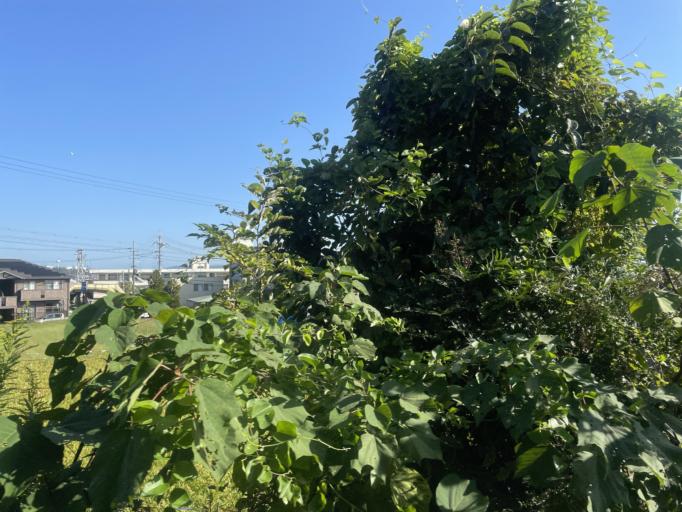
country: JP
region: Osaka
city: Kashihara
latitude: 34.5386
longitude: 135.6872
